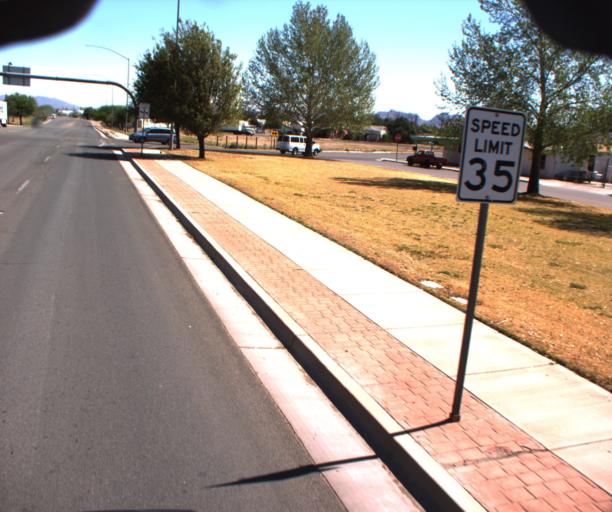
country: US
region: Arizona
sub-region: Cochise County
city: Douglas
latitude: 31.3503
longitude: -109.5545
